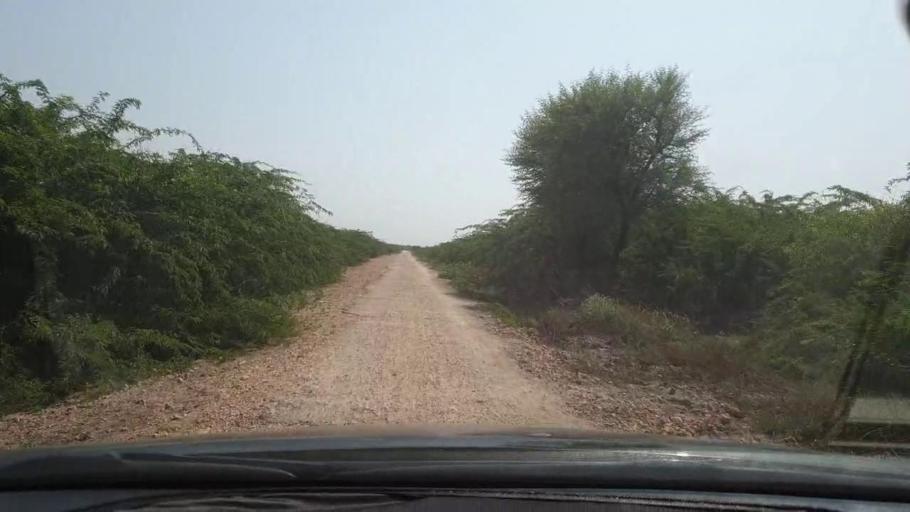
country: PK
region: Sindh
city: Naukot
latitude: 24.8101
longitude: 69.2442
